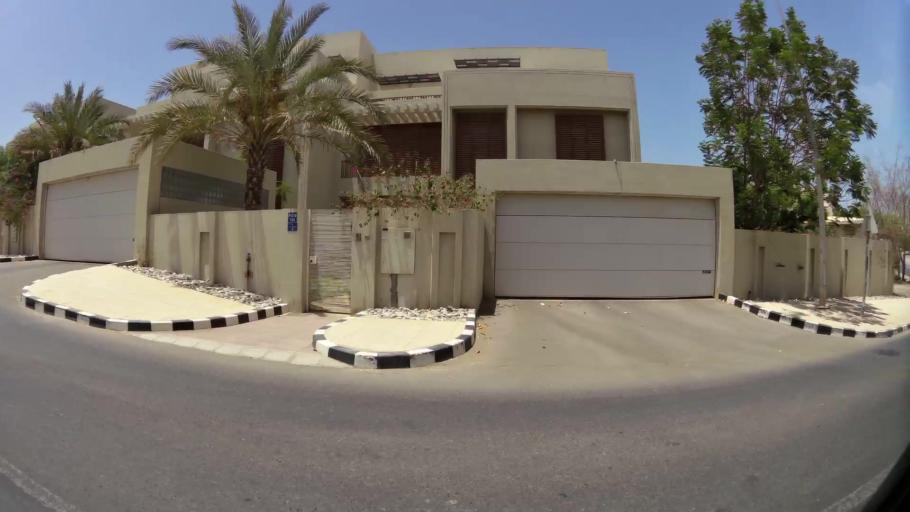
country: OM
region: Muhafazat Masqat
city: Muscat
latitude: 23.6249
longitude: 58.4988
